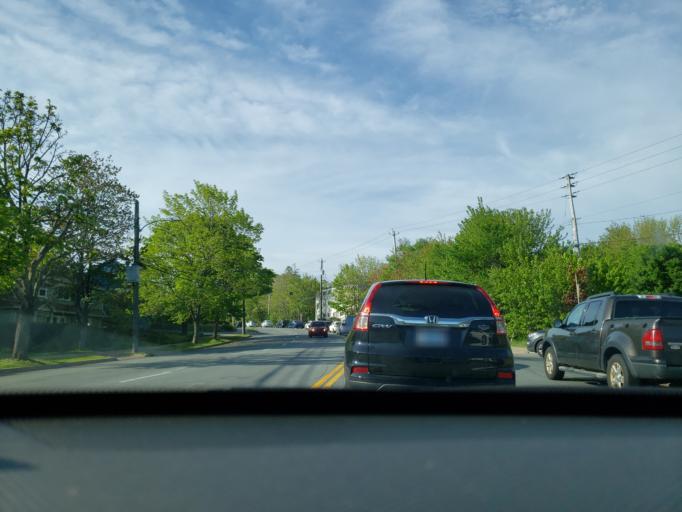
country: CA
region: Nova Scotia
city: Dartmouth
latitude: 44.6508
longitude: -63.6307
